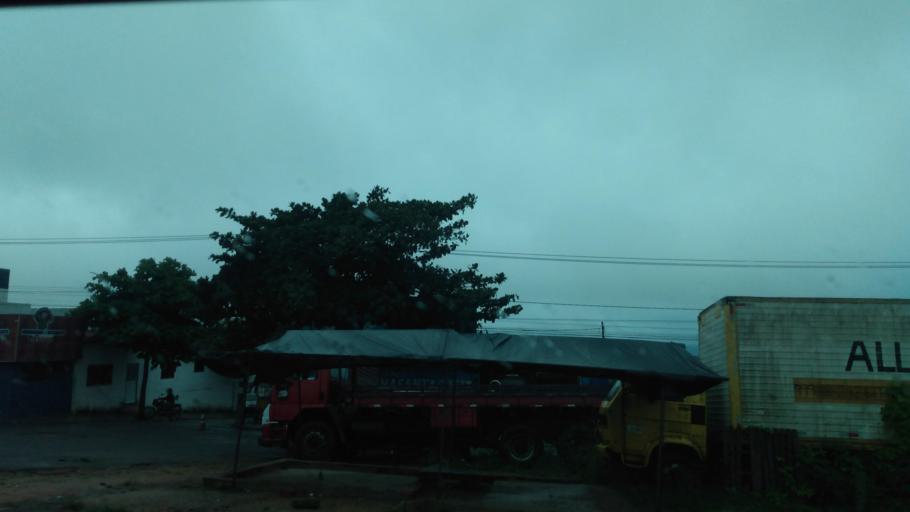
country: BR
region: Pernambuco
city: Garanhuns
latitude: -8.8794
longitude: -36.4955
